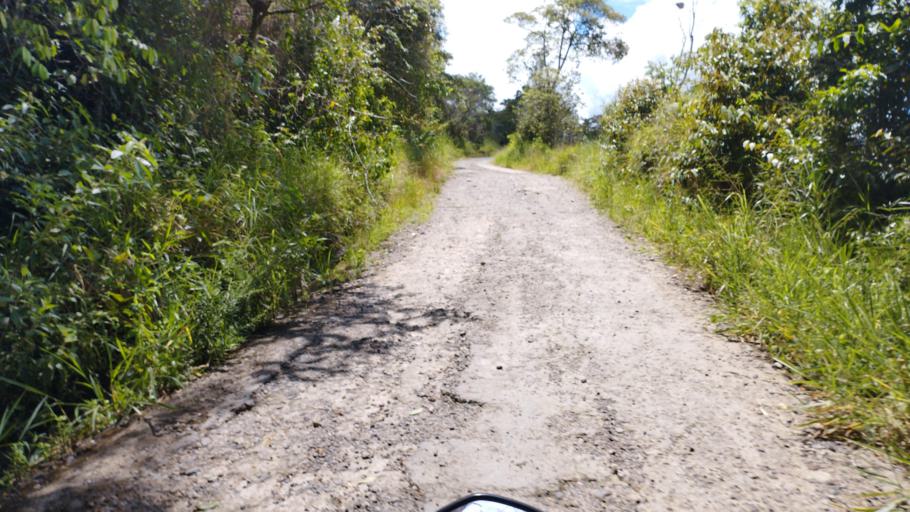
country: CO
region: Boyaca
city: San Luis de Gaceno
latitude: 4.7652
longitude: -73.1336
